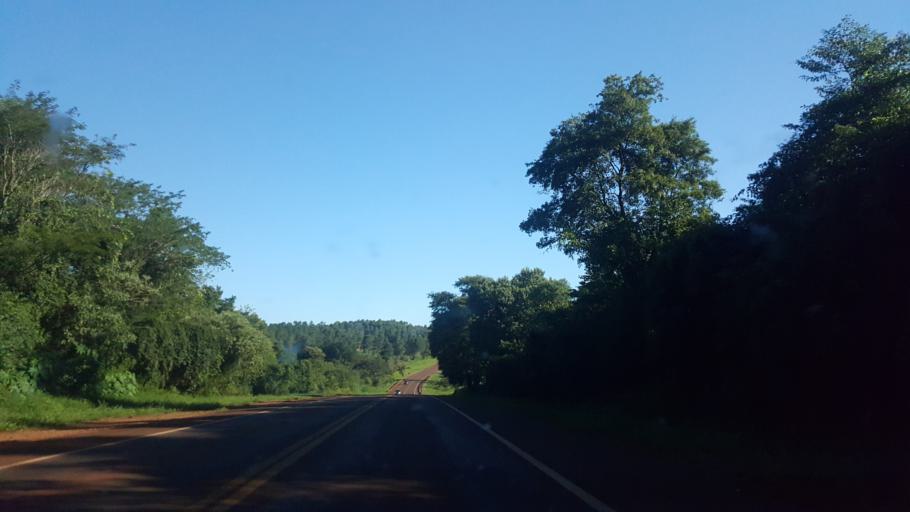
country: AR
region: Misiones
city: Puerto Esperanza
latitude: -26.1614
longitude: -54.5835
